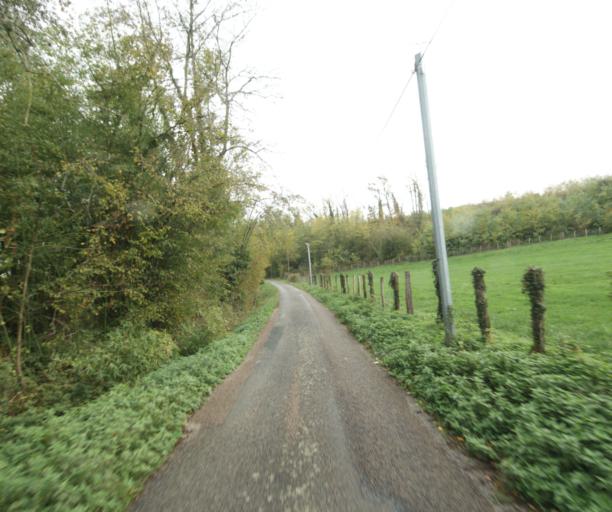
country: FR
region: Rhone-Alpes
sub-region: Departement de l'Ain
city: Pont-de-Vaux
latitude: 46.4716
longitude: 4.8700
